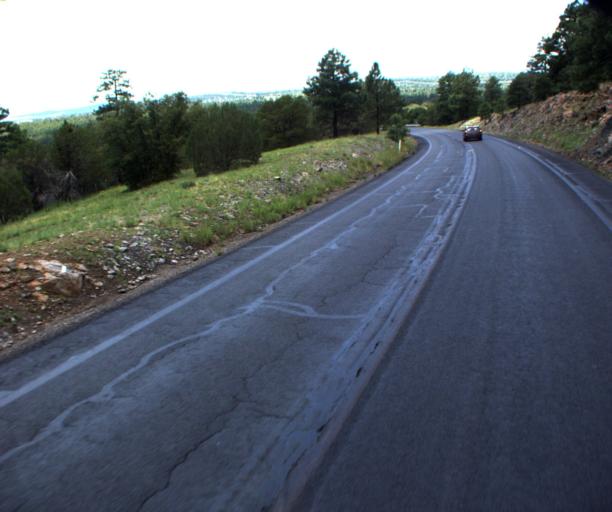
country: US
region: Arizona
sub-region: Gila County
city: Pine
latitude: 34.5168
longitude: -111.4985
